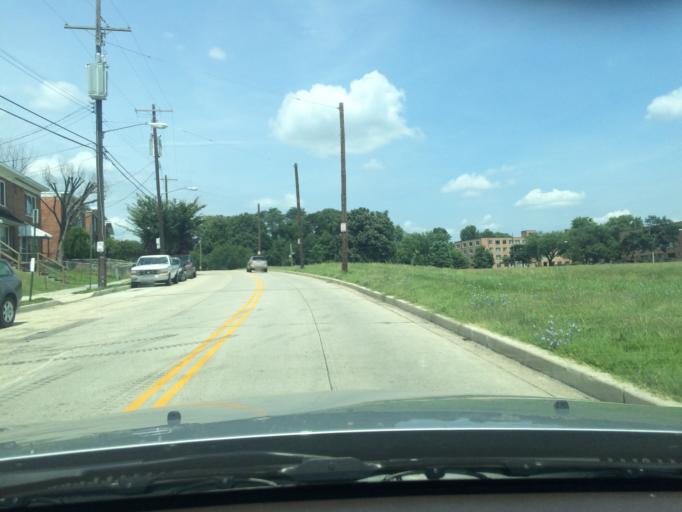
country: US
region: Maryland
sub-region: Prince George's County
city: Chillum
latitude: 38.9521
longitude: -76.9874
